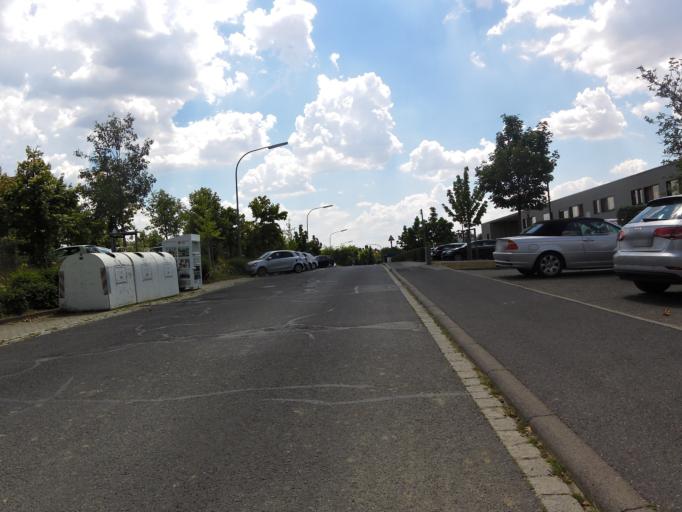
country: DE
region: Bavaria
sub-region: Regierungsbezirk Unterfranken
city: Randersacker
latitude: 49.7386
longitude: 9.9563
